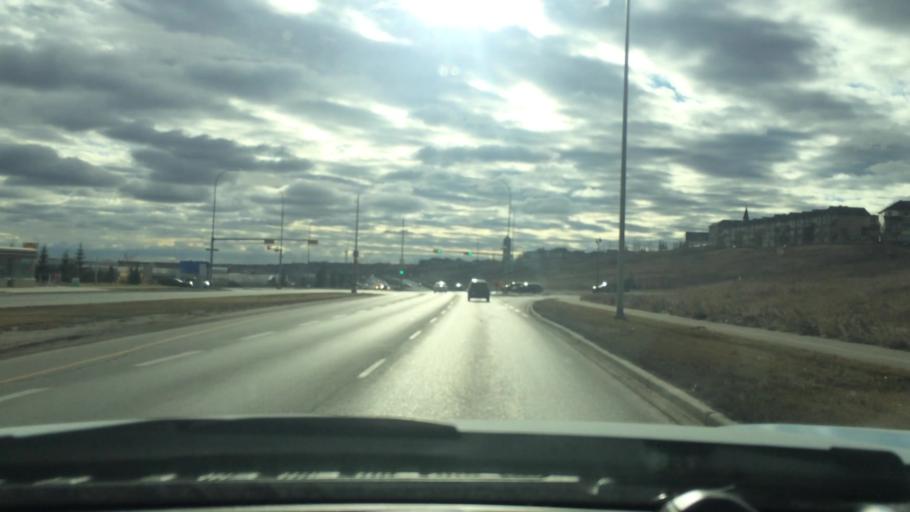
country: CA
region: Alberta
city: Calgary
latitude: 51.1666
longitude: -114.1311
